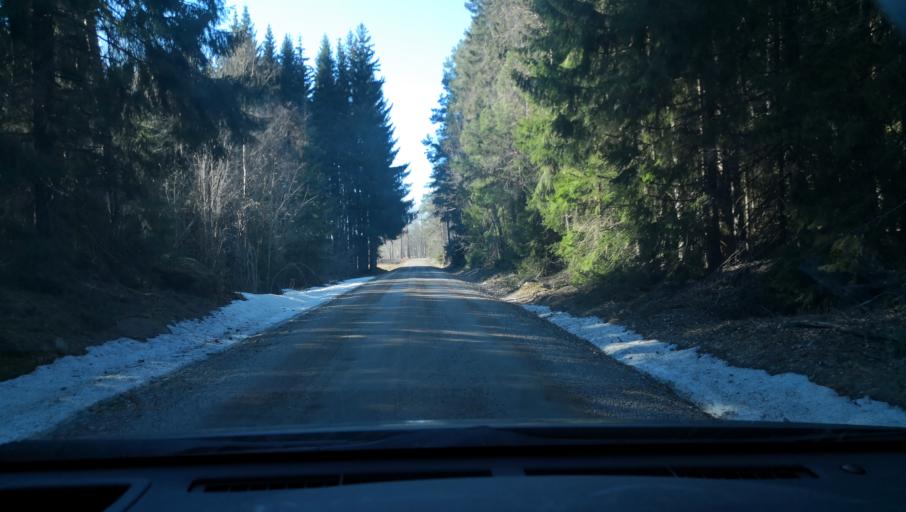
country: SE
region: Vaestmanland
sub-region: Sala Kommun
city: Sala
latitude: 60.1447
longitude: 16.6459
